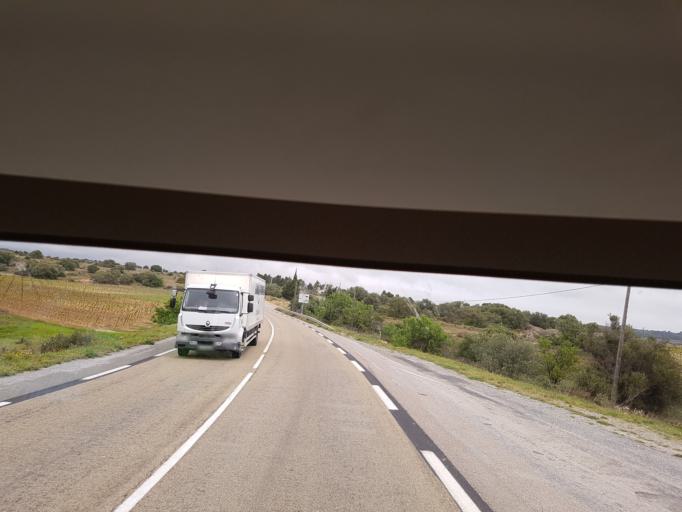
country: FR
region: Languedoc-Roussillon
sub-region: Departement de l'Aude
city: Leucate
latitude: 42.9027
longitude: 3.0011
